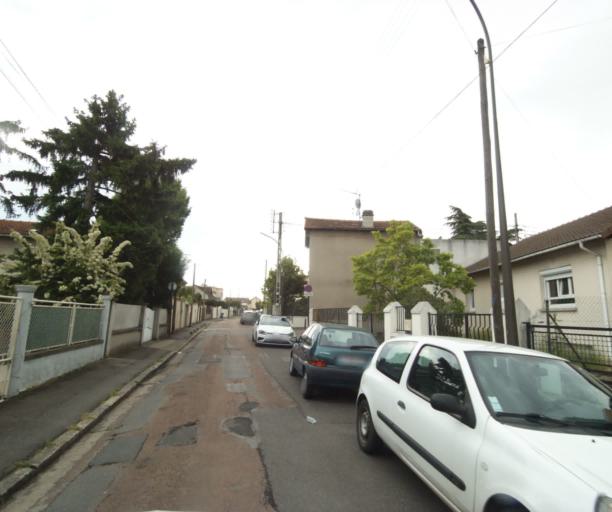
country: FR
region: Ile-de-France
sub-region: Departement du Val-d'Oise
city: Bezons
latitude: 48.9429
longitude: 2.2223
